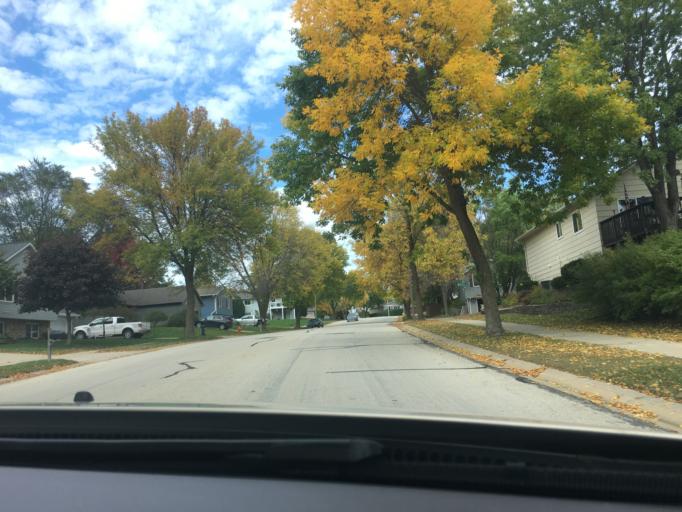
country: US
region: Minnesota
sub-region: Olmsted County
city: Rochester
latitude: 44.0803
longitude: -92.5220
